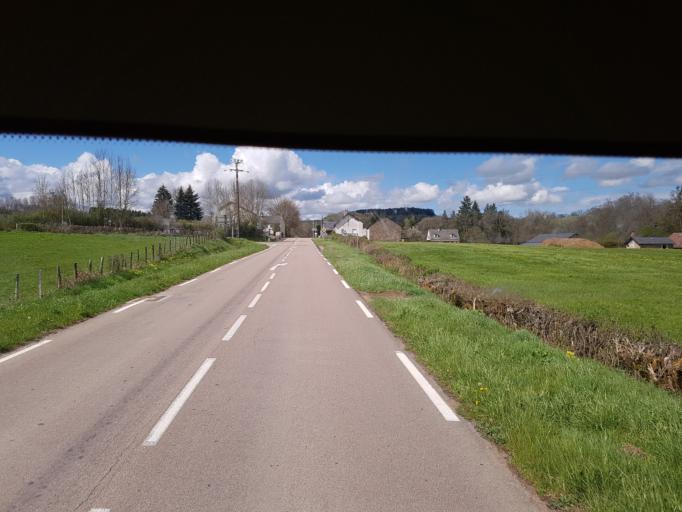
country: FR
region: Bourgogne
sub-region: Departement de la Cote-d'Or
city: Saulieu
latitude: 47.1102
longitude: 4.2281
